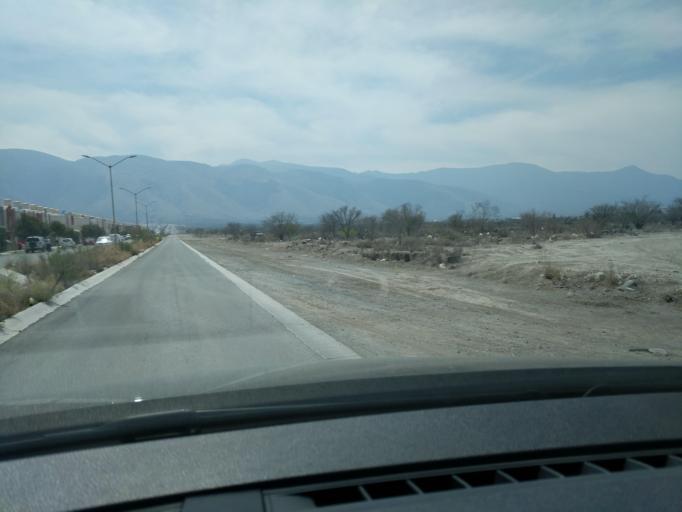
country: MX
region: Coahuila
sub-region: Arteaga
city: Arteaga
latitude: 25.4268
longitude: -100.9130
